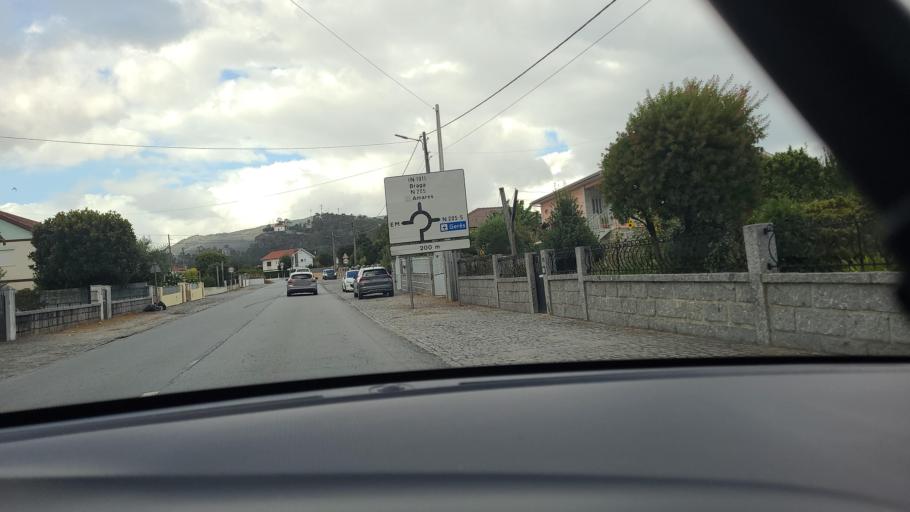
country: PT
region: Braga
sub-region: Amares
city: Amares
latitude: 41.6260
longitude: -8.3417
